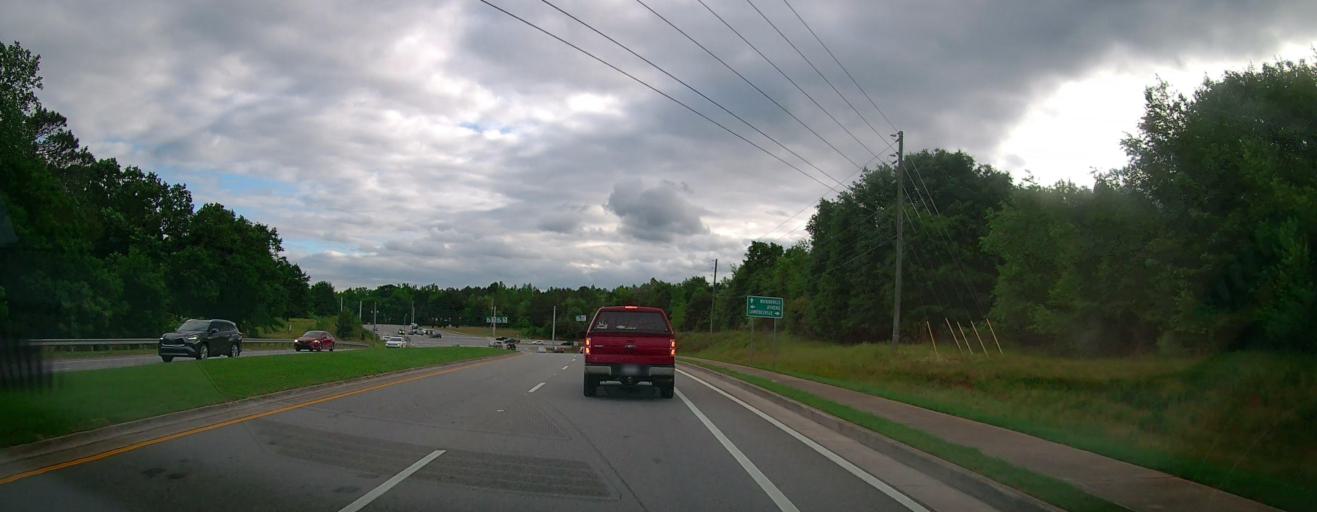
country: US
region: Georgia
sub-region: Oconee County
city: Watkinsville
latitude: 33.9135
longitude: -83.4640
